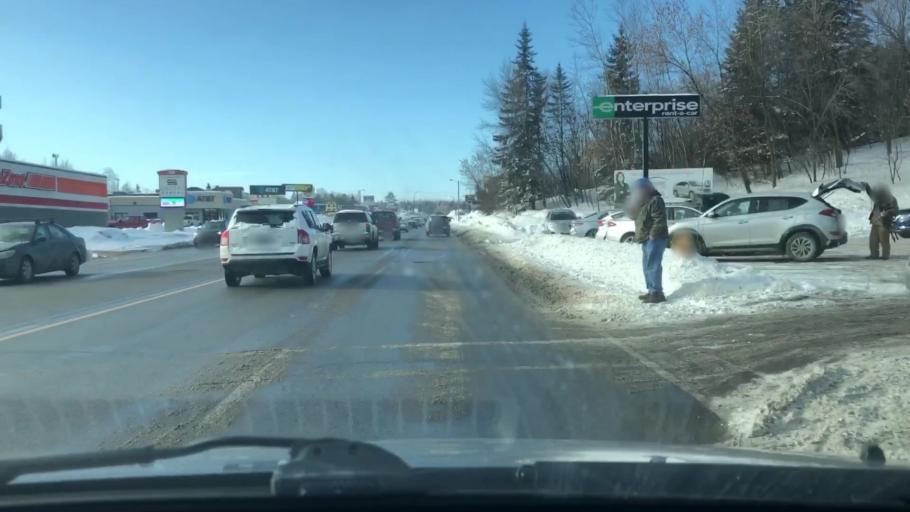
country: US
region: Minnesota
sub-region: Saint Louis County
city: Duluth
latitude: 46.8005
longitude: -92.1265
